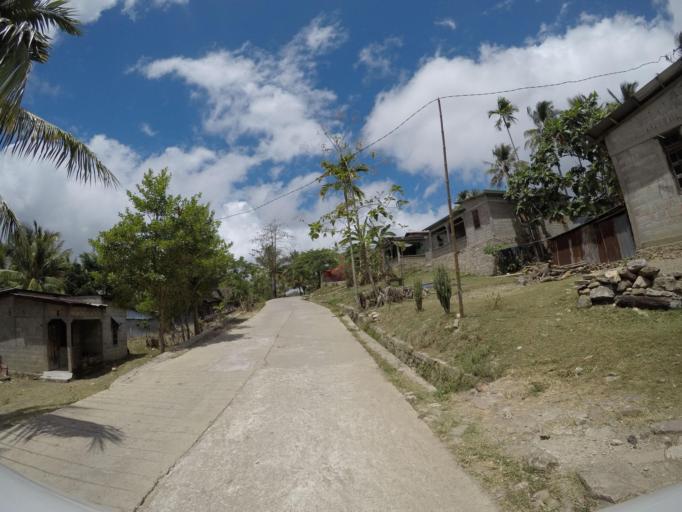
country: TL
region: Lautem
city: Lospalos
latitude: -8.5461
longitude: 126.8327
